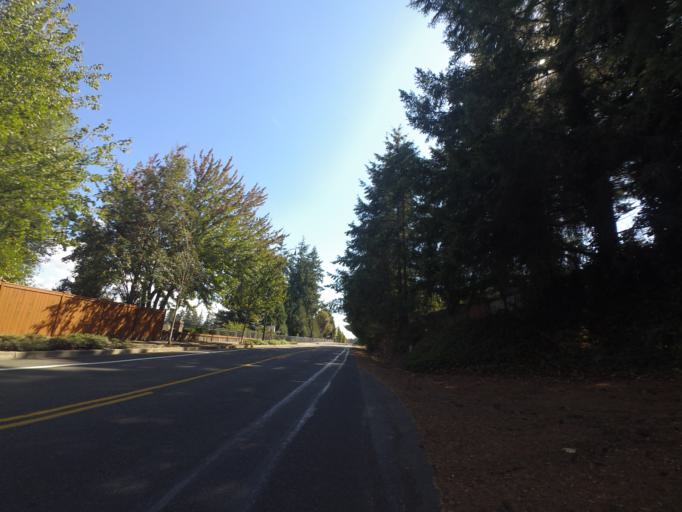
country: US
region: Washington
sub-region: Pierce County
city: Fircrest
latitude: 47.2121
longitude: -122.5160
